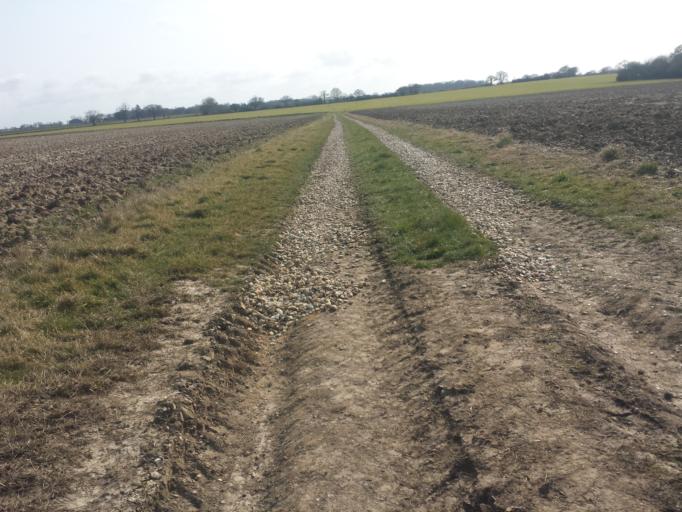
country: GB
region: England
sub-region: Essex
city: Mistley
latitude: 51.9075
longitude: 1.1519
